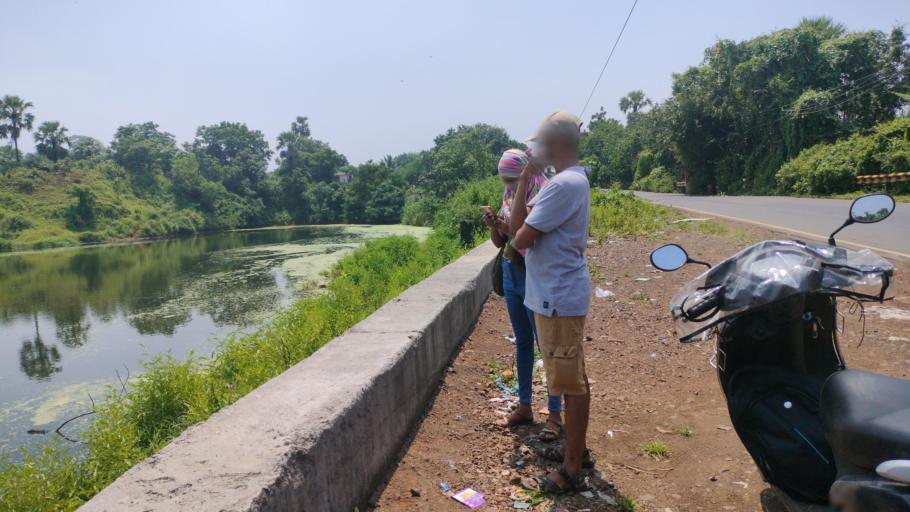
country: IN
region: Maharashtra
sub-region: Thane
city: Virar
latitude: 19.3848
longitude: 72.7844
